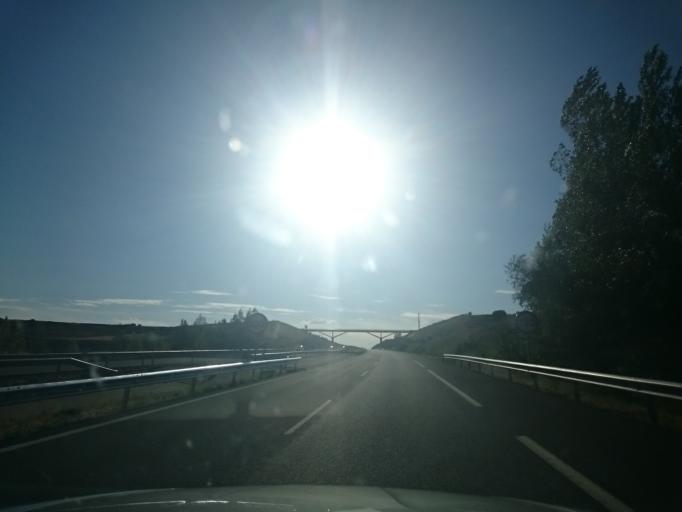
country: ES
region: Castille and Leon
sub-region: Provincia de Burgos
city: Villanueva de Argano
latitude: 42.3873
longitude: -3.9776
